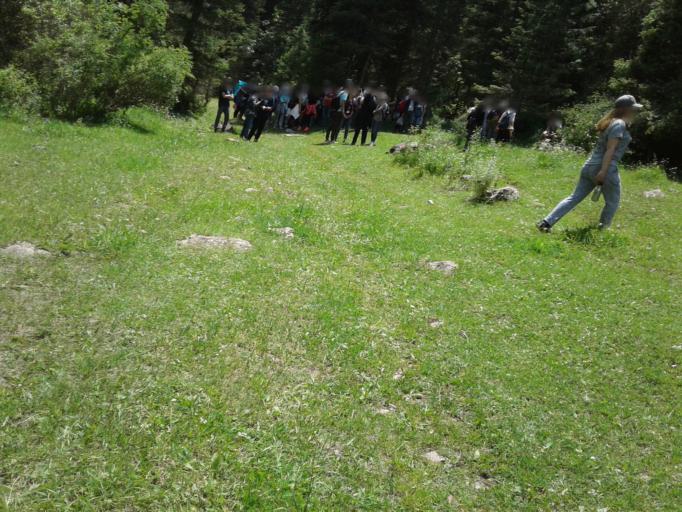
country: KG
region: Naryn
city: Naryn
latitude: 41.4175
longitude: 76.1862
